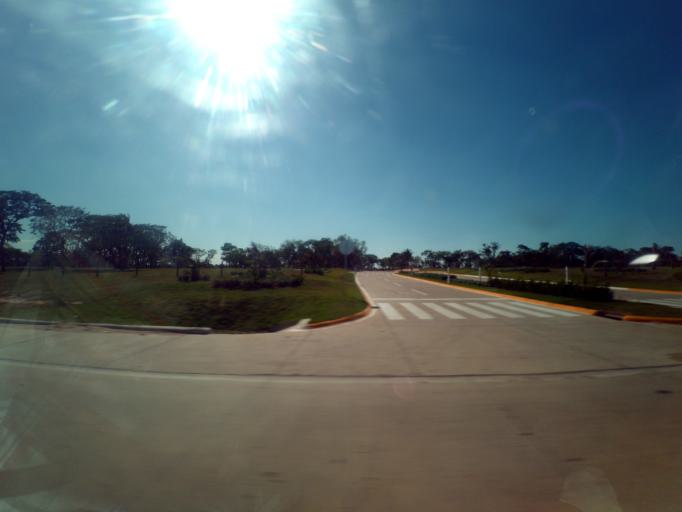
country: BO
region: Santa Cruz
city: Santa Cruz de la Sierra
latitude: -17.7774
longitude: -63.2480
